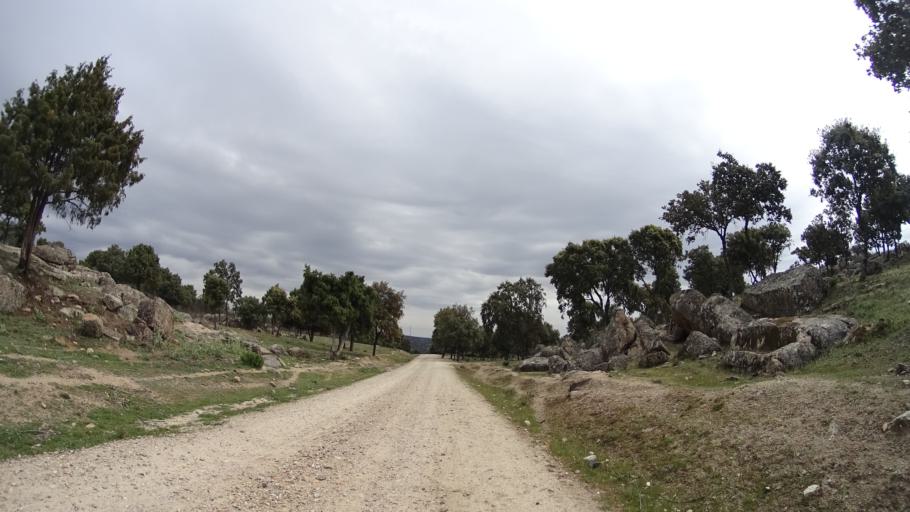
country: ES
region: Madrid
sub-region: Provincia de Madrid
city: Hoyo de Manzanares
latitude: 40.6004
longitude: -3.8821
